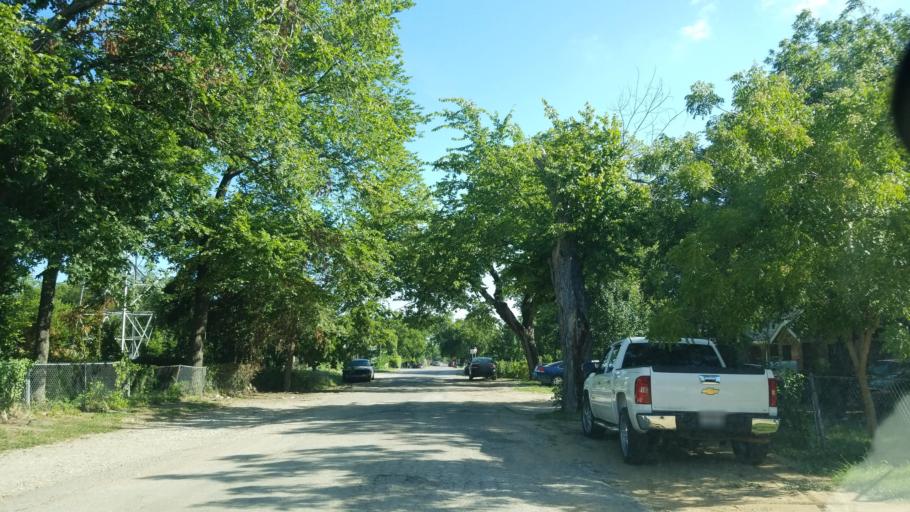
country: US
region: Texas
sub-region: Dallas County
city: Dallas
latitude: 32.7159
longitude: -96.8097
